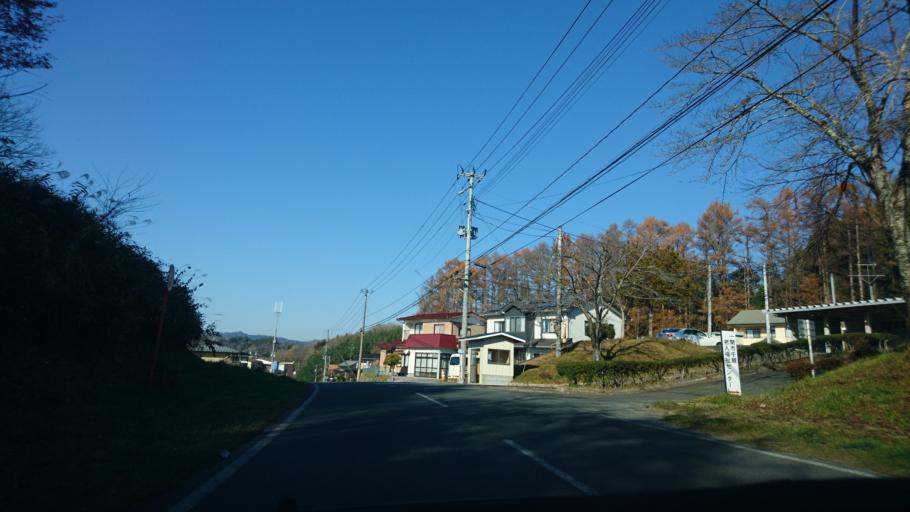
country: JP
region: Iwate
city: Ichinoseki
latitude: 38.9133
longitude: 141.3449
